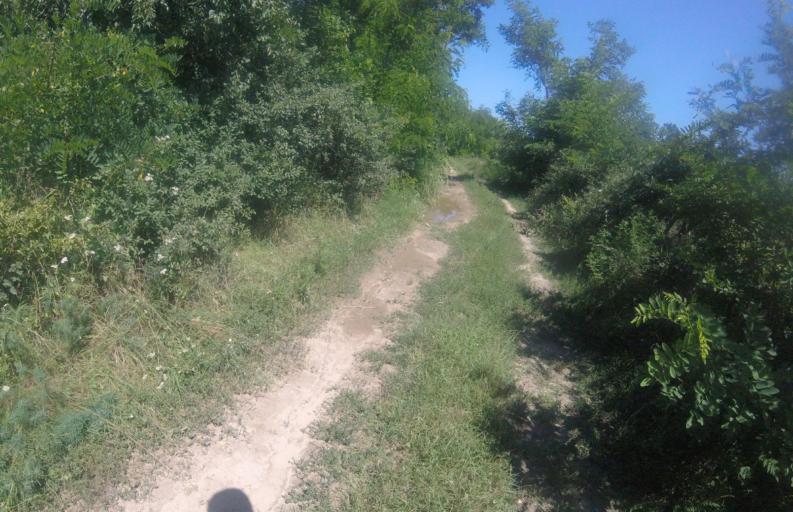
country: HU
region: Zala
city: Heviz
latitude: 46.8206
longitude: 17.1945
